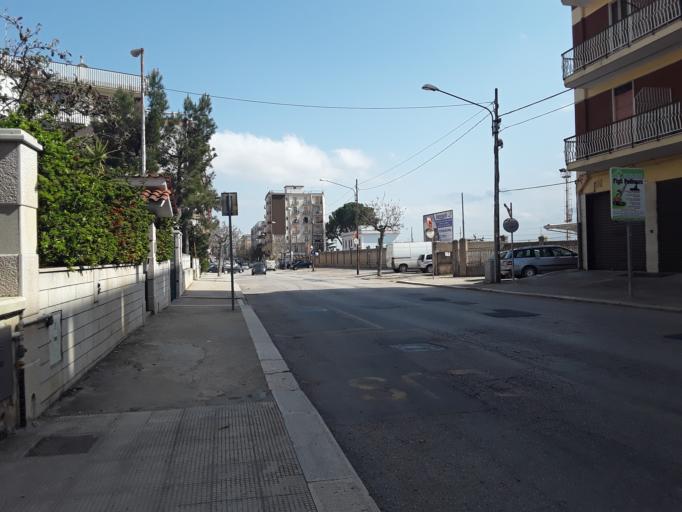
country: IT
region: Apulia
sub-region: Provincia di Bari
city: Ruvo di Puglia
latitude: 41.1163
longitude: 16.4782
